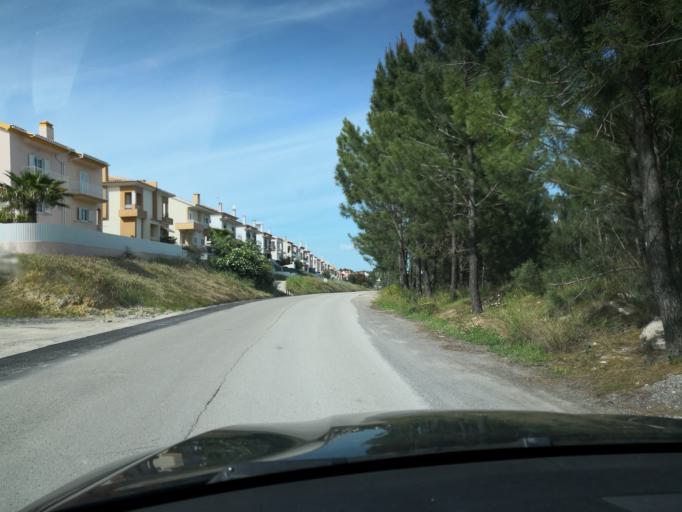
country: PT
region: Setubal
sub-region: Barreiro
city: Santo Antonio da Charneca
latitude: 38.5494
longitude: -9.0422
